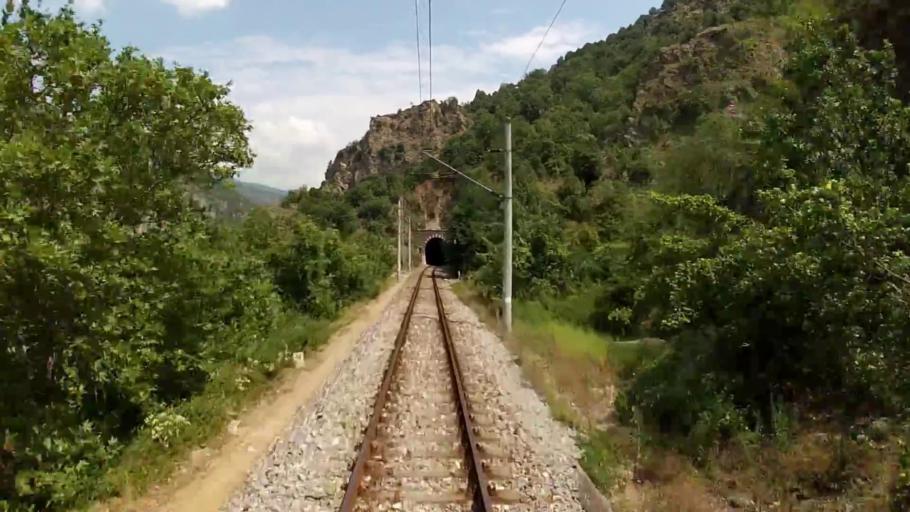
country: BG
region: Blagoevgrad
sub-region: Obshtina Kresna
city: Kresna
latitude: 41.7436
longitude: 23.1627
